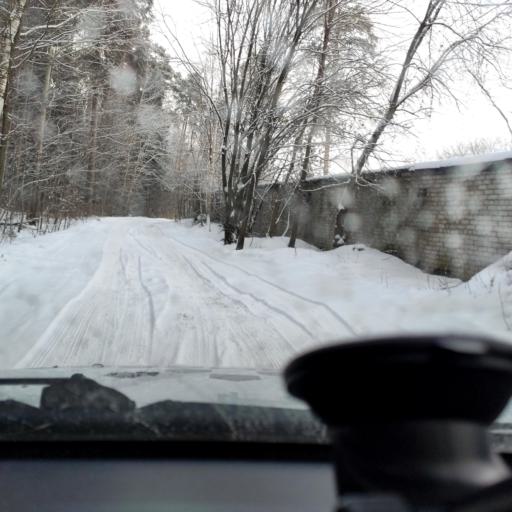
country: RU
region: Perm
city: Kondratovo
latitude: 57.9736
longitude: 56.1492
